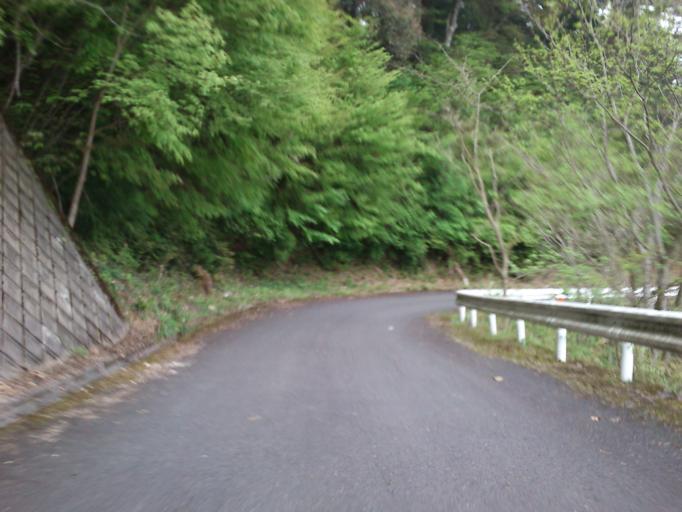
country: JP
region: Kyoto
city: Maizuru
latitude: 35.3862
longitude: 135.4424
